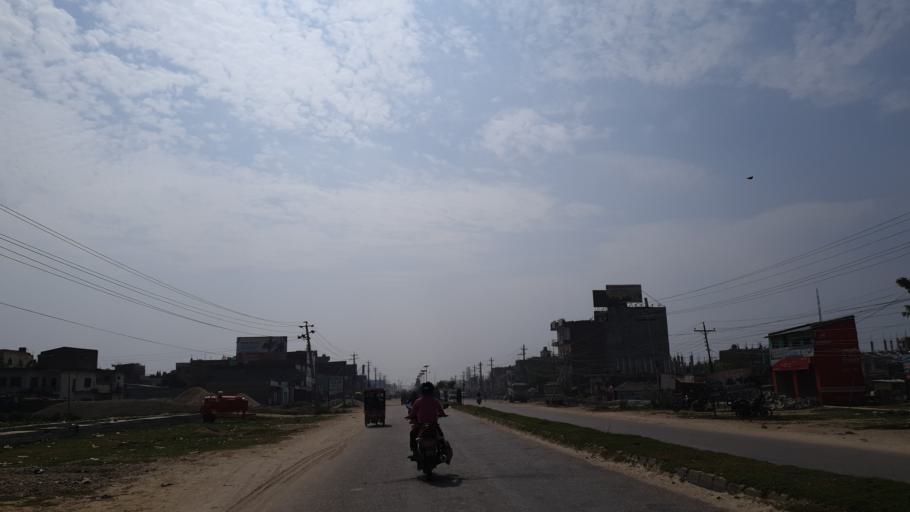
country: NP
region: Central Region
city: Janakpur
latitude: 26.7462
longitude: 85.9230
